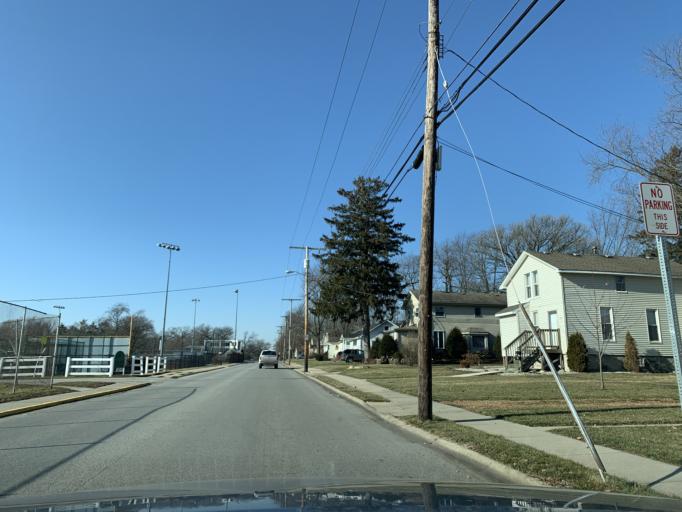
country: US
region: Indiana
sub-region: Lake County
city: Crown Point
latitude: 41.4203
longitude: -87.3668
